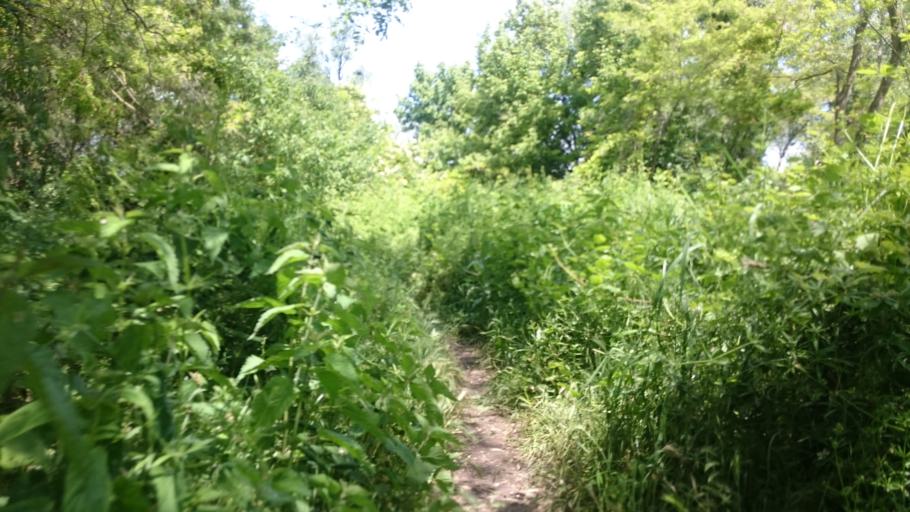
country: IT
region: Lombardy
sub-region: Provincia di Mantova
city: Mantova
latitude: 45.1435
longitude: 10.8062
